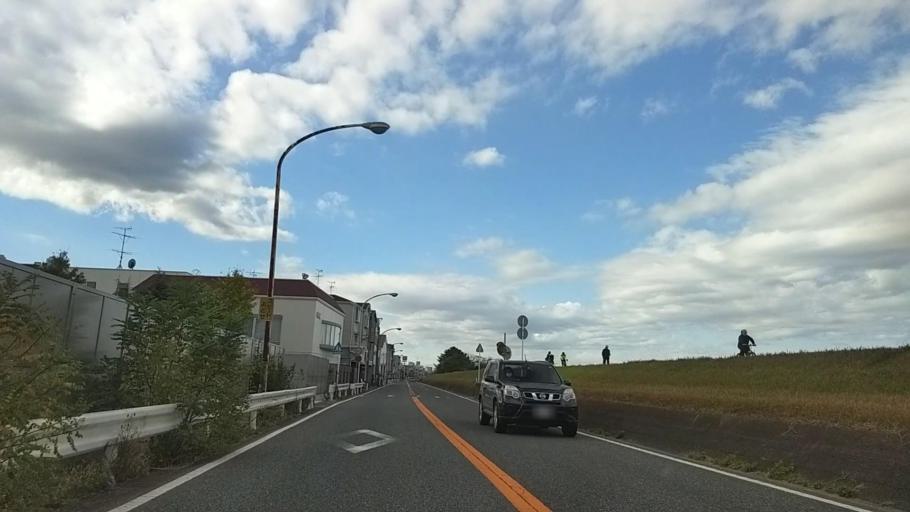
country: JP
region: Tokyo
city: Chofugaoka
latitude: 35.6177
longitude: 139.5853
